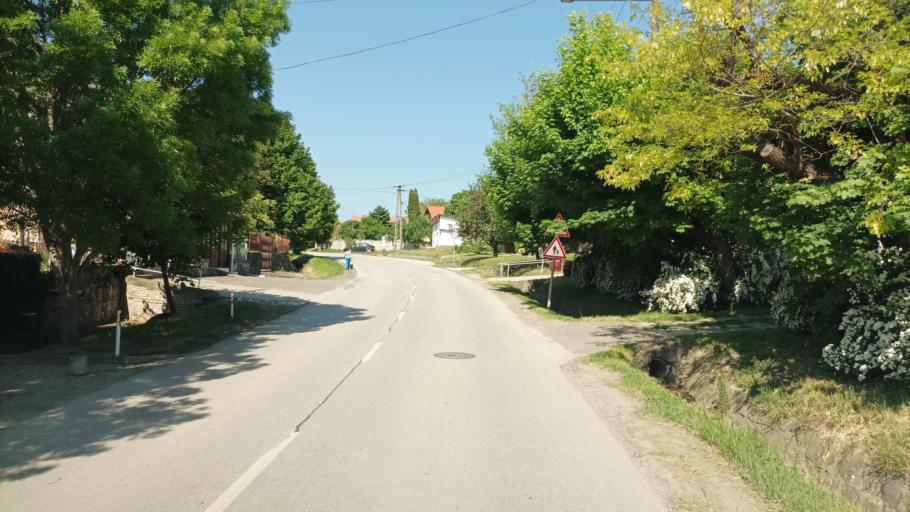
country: HU
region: Pest
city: Gomba
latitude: 47.3720
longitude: 19.5280
